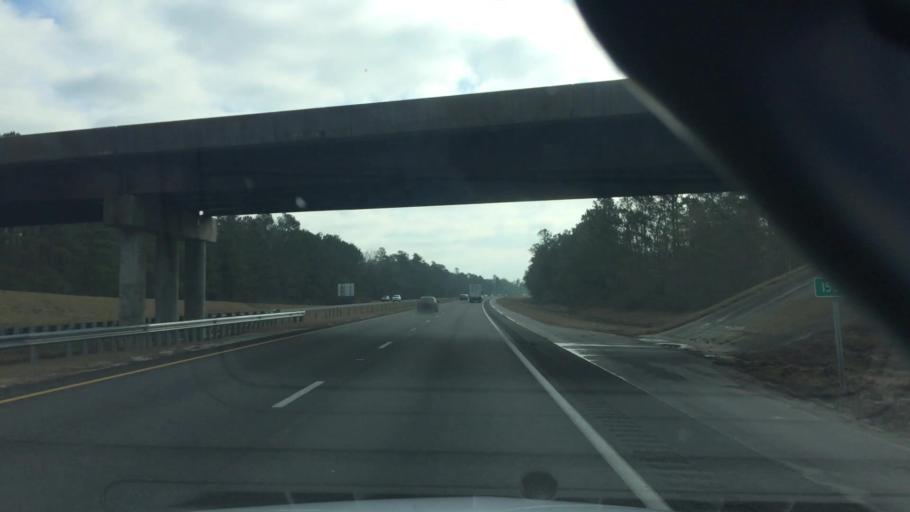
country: US
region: North Carolina
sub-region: Pender County
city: Burgaw
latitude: 34.5657
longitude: -77.8978
